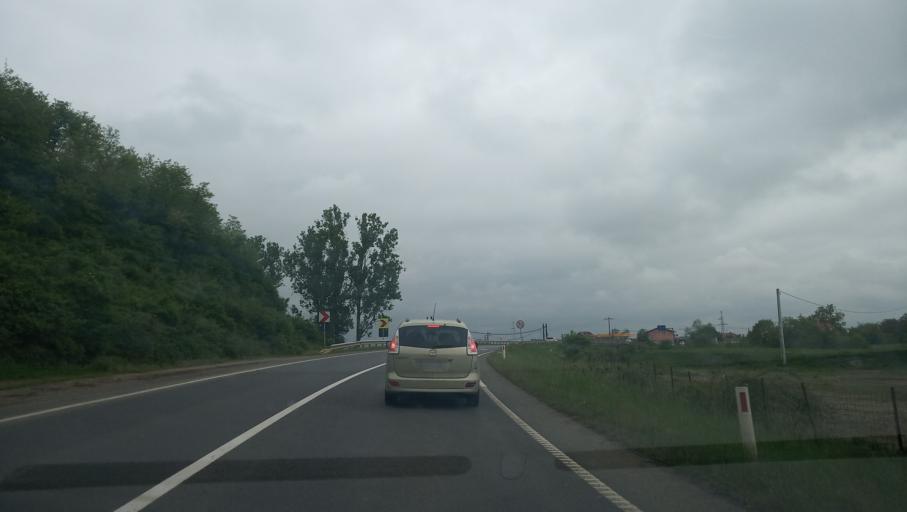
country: RO
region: Alba
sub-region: Comuna Sibot
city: Sibot
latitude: 45.9226
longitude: 23.3493
